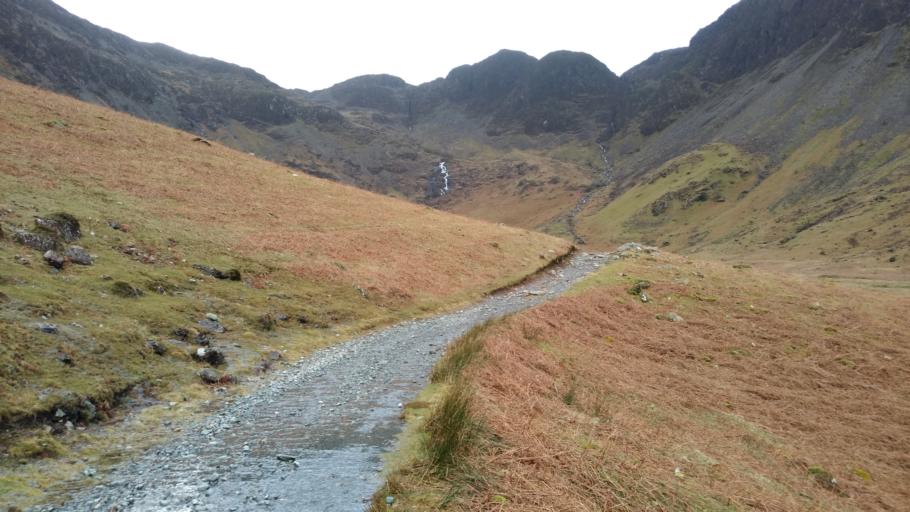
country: GB
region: England
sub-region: Cumbria
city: Keswick
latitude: 54.5164
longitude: -3.2432
